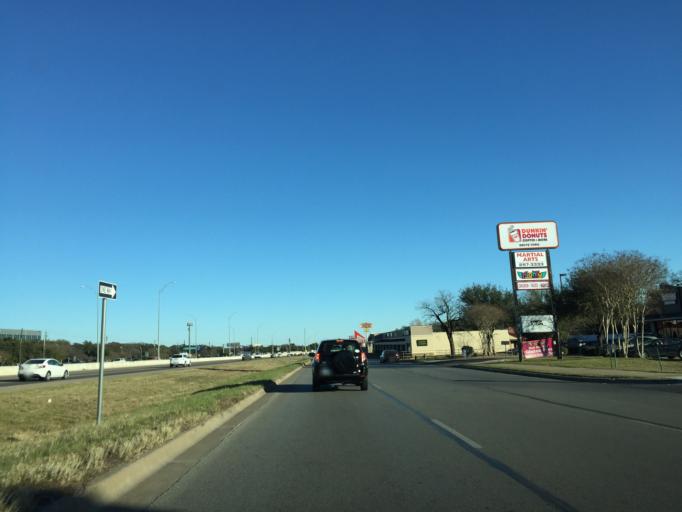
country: US
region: Texas
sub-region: Williamson County
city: Jollyville
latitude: 30.4263
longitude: -97.7541
